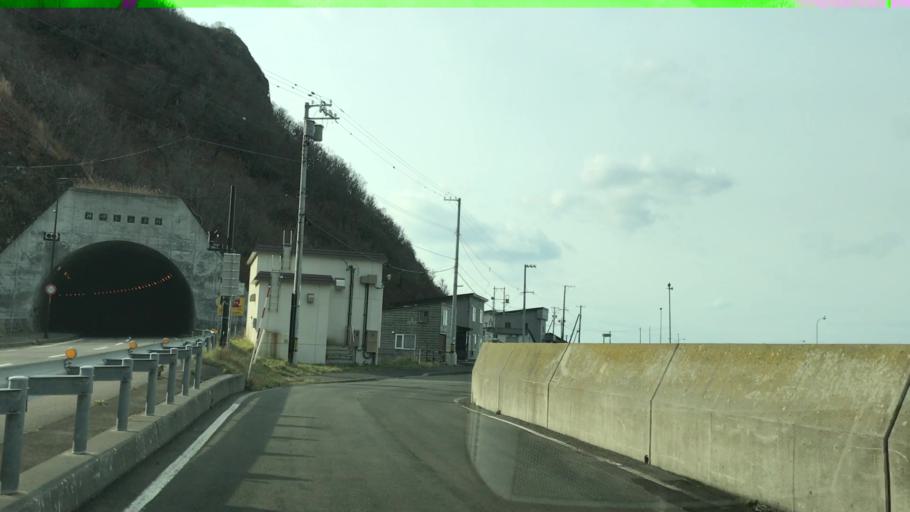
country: JP
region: Hokkaido
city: Iwanai
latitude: 43.3148
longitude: 140.3595
